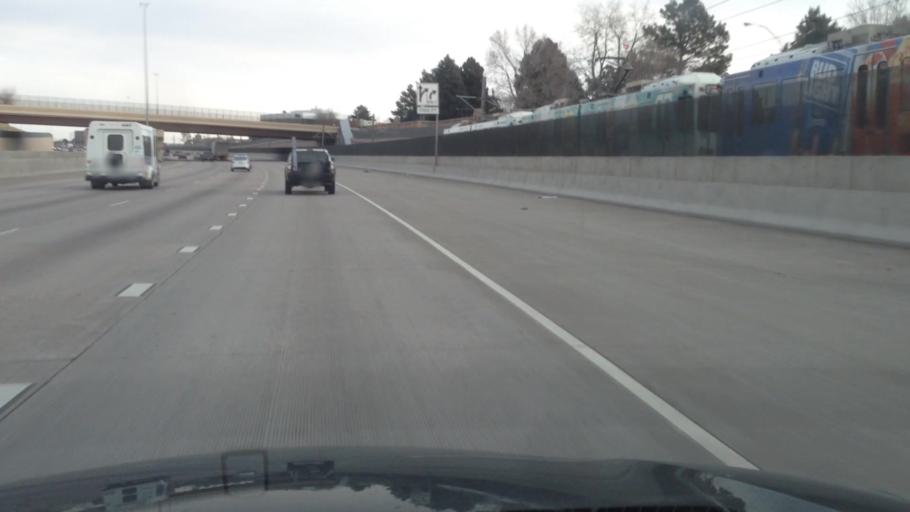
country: US
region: Colorado
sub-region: Adams County
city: Aurora
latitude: 39.6658
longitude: -104.8308
